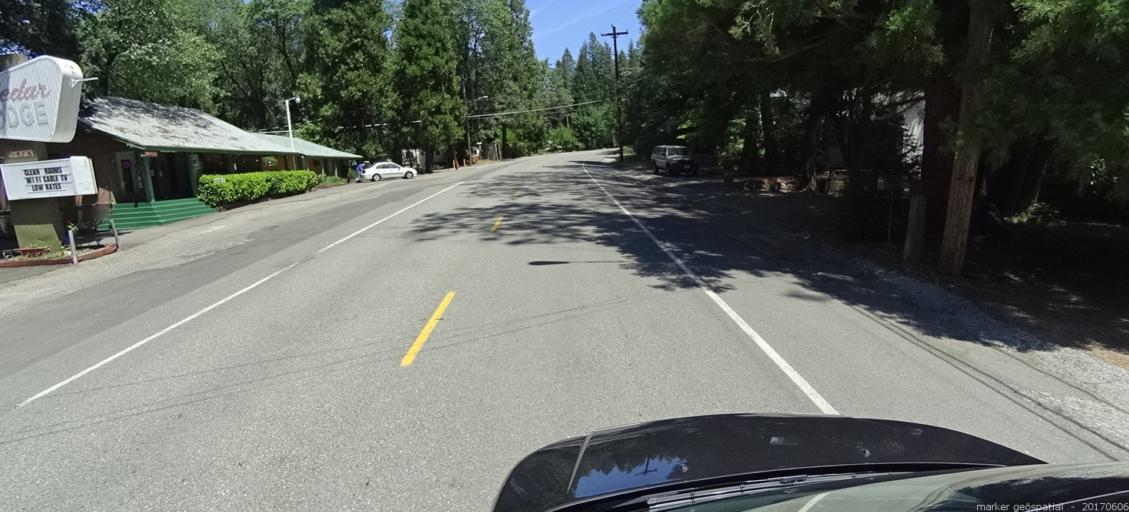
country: US
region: California
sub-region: Siskiyou County
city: Dunsmuir
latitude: 41.2341
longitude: -122.2731
